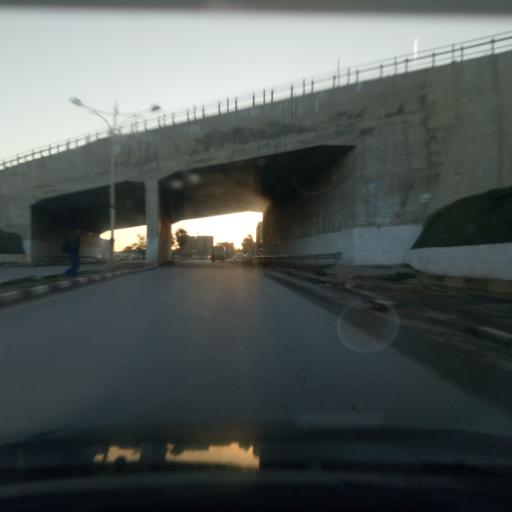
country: DZ
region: Tipaza
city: Bou Ismail
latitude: 36.6405
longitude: 2.7057
